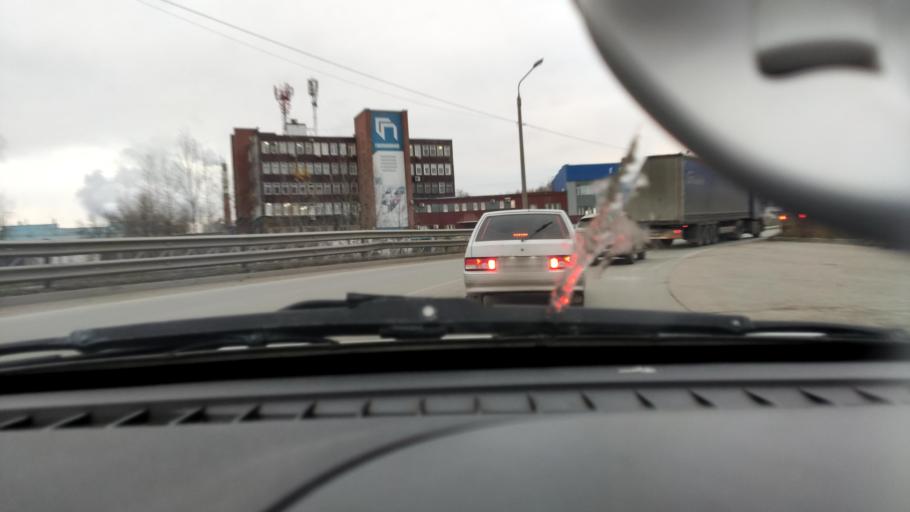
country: RU
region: Perm
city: Perm
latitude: 57.9622
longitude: 56.2065
